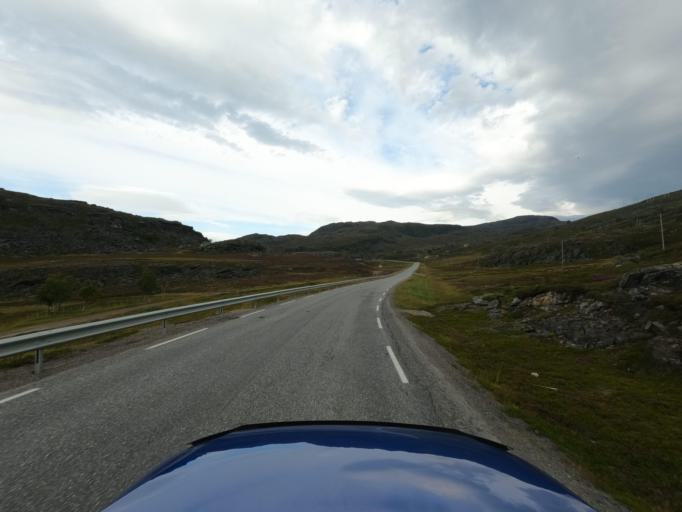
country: NO
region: Finnmark Fylke
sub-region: Hammerfest
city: Rypefjord
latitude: 70.5960
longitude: 23.6813
